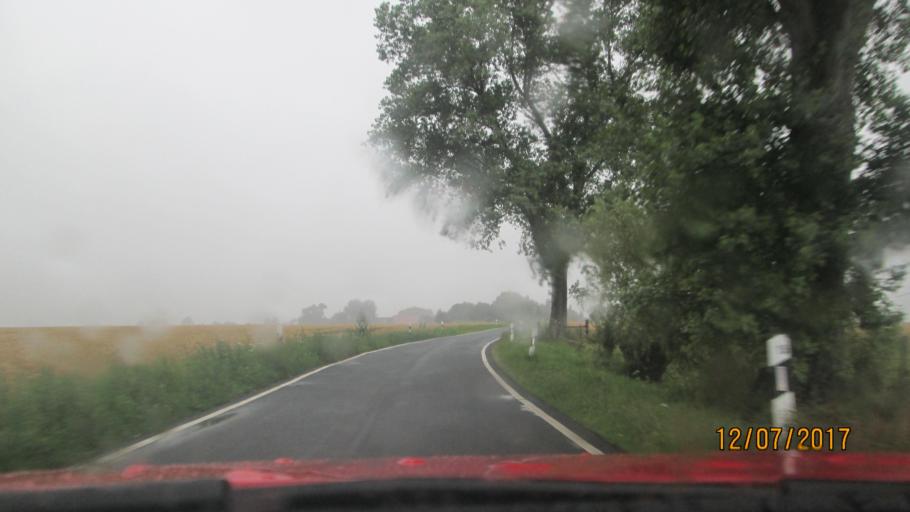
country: DE
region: Lower Saxony
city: Lehre
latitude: 52.3760
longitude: 10.6668
